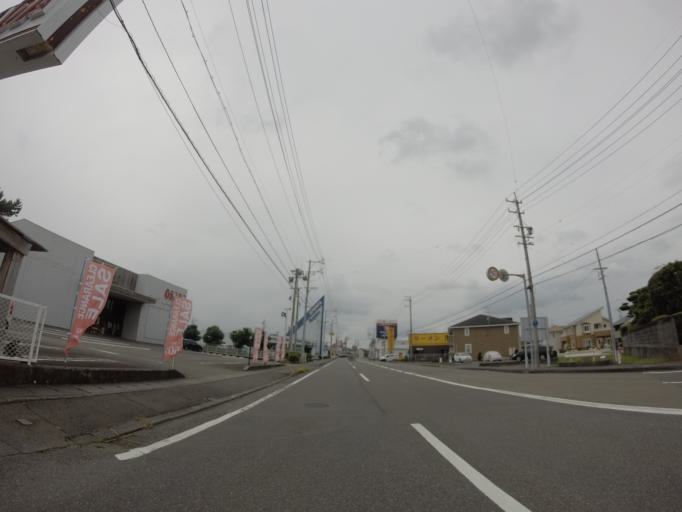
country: JP
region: Shizuoka
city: Fujieda
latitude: 34.8552
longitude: 138.2614
